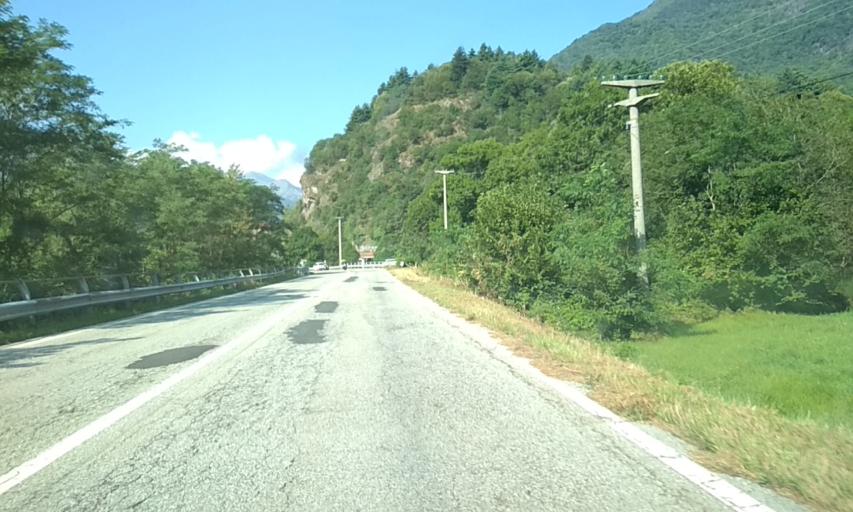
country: IT
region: Piedmont
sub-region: Provincia di Torino
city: Sparone
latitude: 45.4153
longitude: 7.5544
